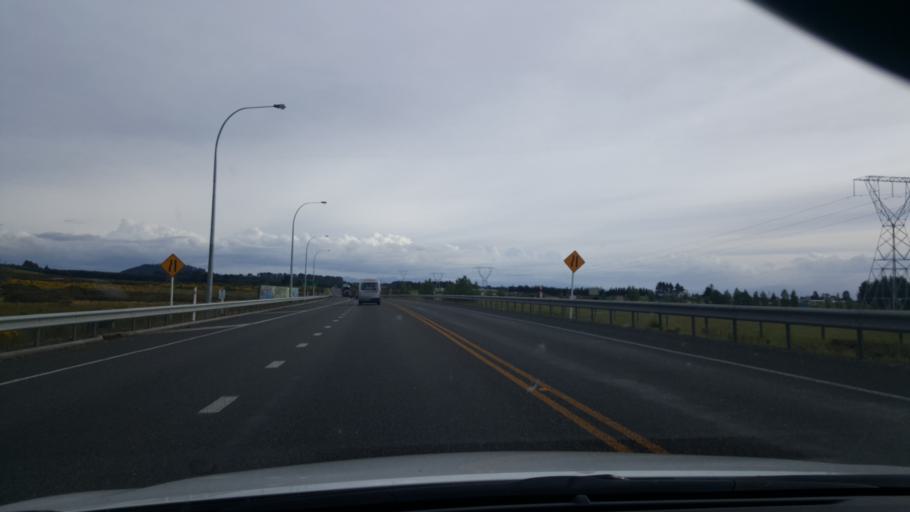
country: NZ
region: Waikato
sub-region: Taupo District
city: Taupo
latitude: -38.6857
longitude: 176.1141
